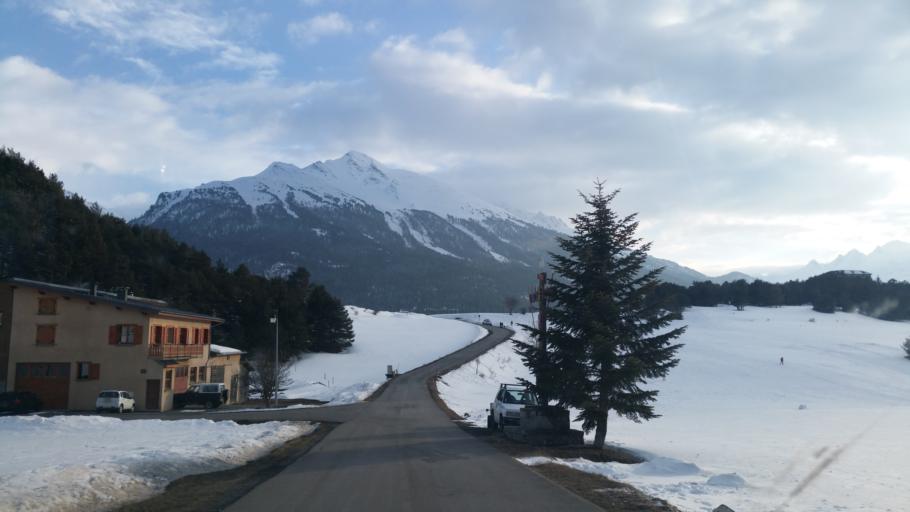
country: FR
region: Rhone-Alpes
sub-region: Departement de la Savoie
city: Modane
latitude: 45.2248
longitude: 6.7410
